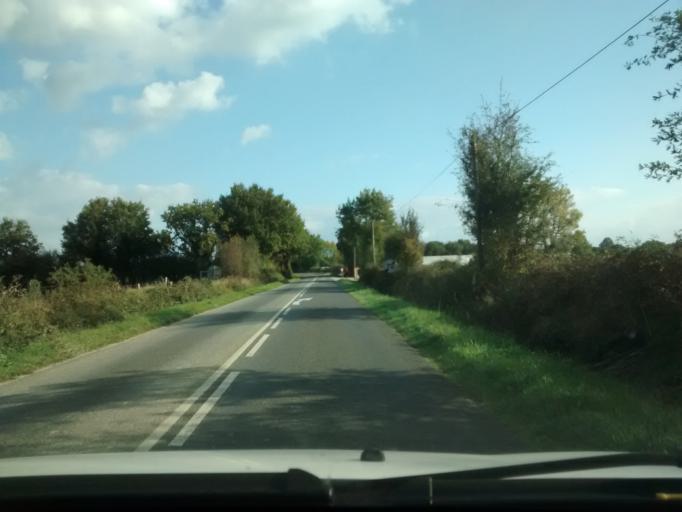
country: FR
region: Pays de la Loire
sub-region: Departement de la Loire-Atlantique
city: Sautron
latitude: 47.2857
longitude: -1.6533
